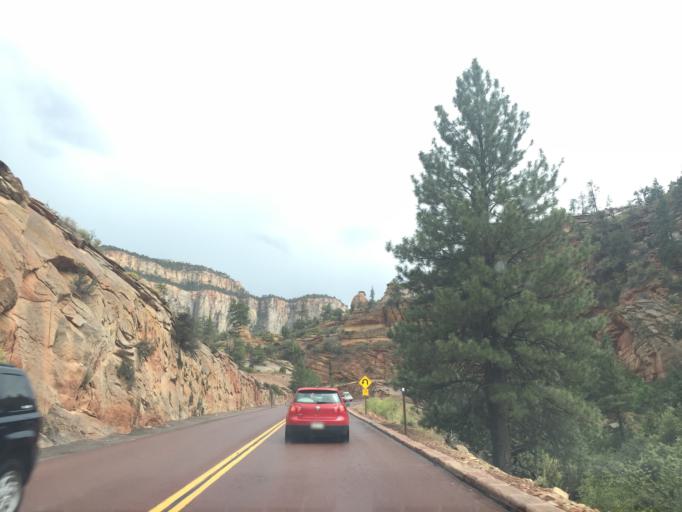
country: US
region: Utah
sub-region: Washington County
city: Hildale
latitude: 37.2234
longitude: -112.8997
